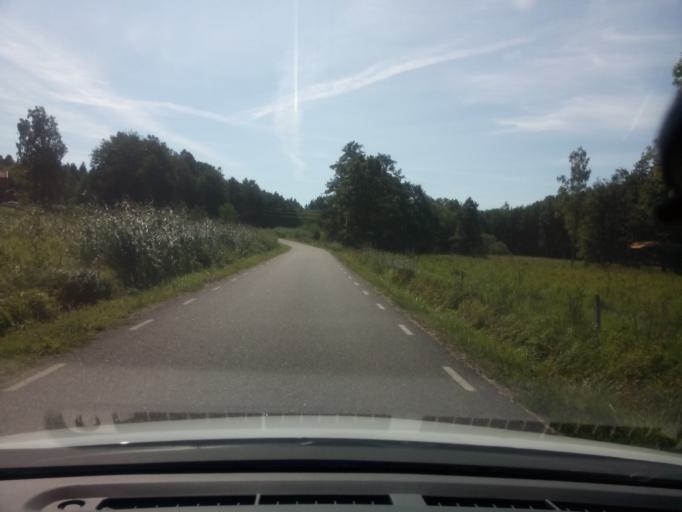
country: SE
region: Soedermanland
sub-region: Trosa Kommun
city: Trosa
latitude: 58.8051
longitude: 17.3644
